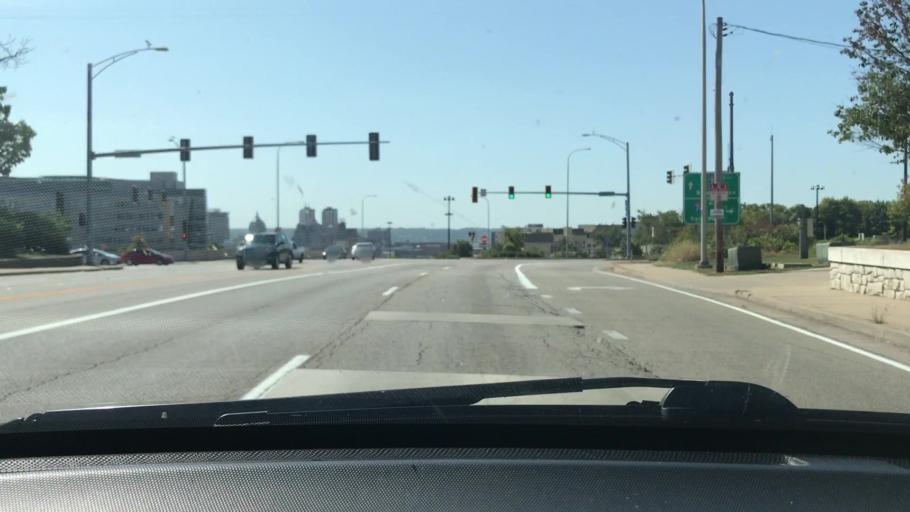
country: US
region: Illinois
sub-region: Peoria County
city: Peoria
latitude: 40.7057
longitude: -89.5941
